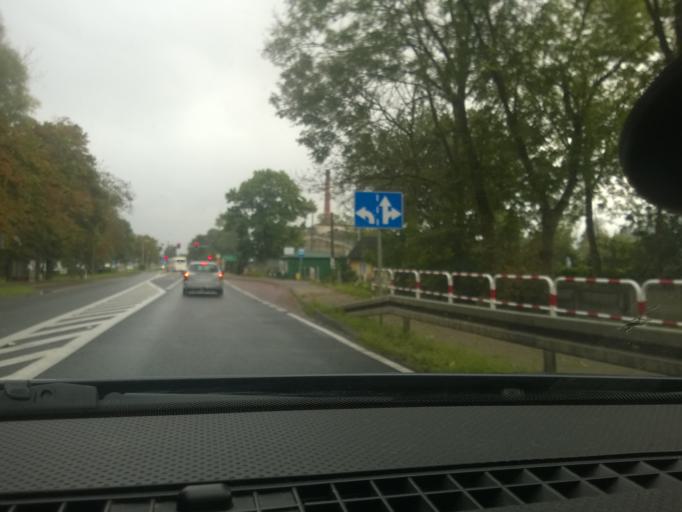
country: PL
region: Greater Poland Voivodeship
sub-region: Powiat kaliski
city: Kozminek
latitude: 51.6867
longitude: 18.3275
